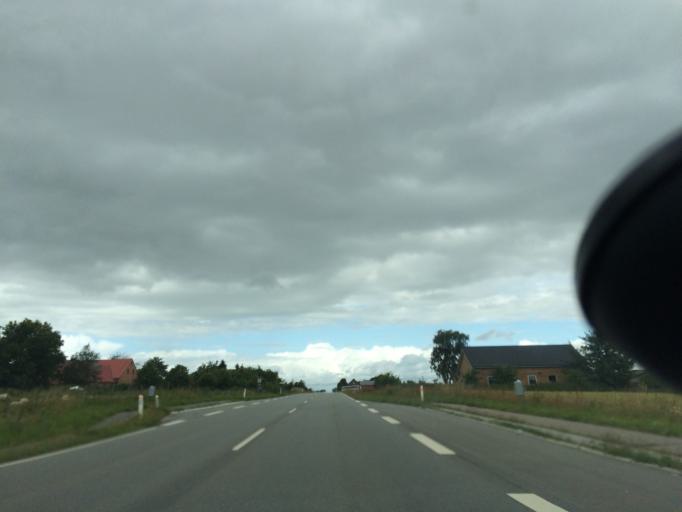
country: DK
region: Central Jutland
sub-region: Skanderborg Kommune
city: Galten
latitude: 56.1486
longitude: 9.8460
